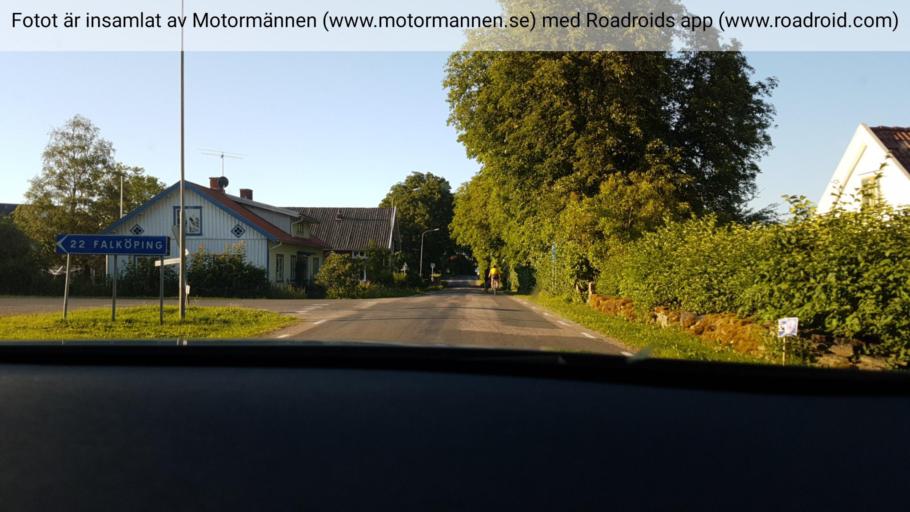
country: SE
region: Vaestra Goetaland
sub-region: Skovde Kommun
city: Skultorp
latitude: 58.2917
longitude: 13.8002
